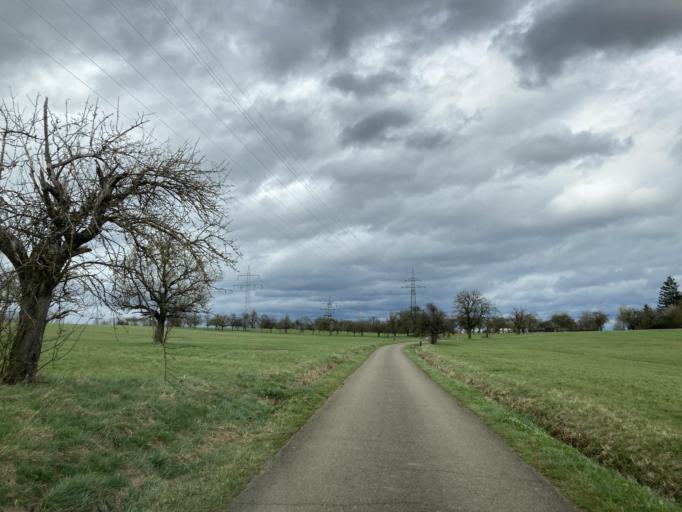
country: DE
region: Baden-Wuerttemberg
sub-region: Tuebingen Region
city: Gomaringen
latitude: 48.4802
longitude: 9.1272
